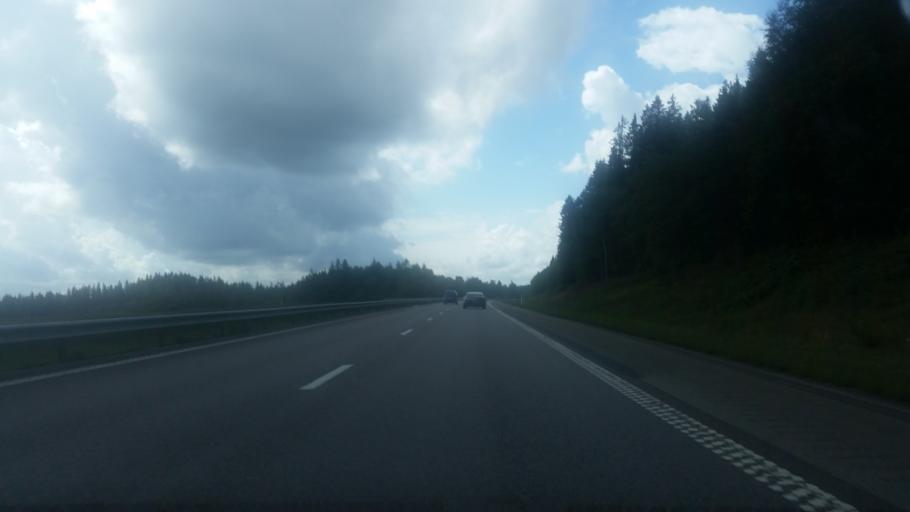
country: SE
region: Vaestra Goetaland
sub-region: Boras Kommun
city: Sandared
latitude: 57.6891
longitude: 12.7936
